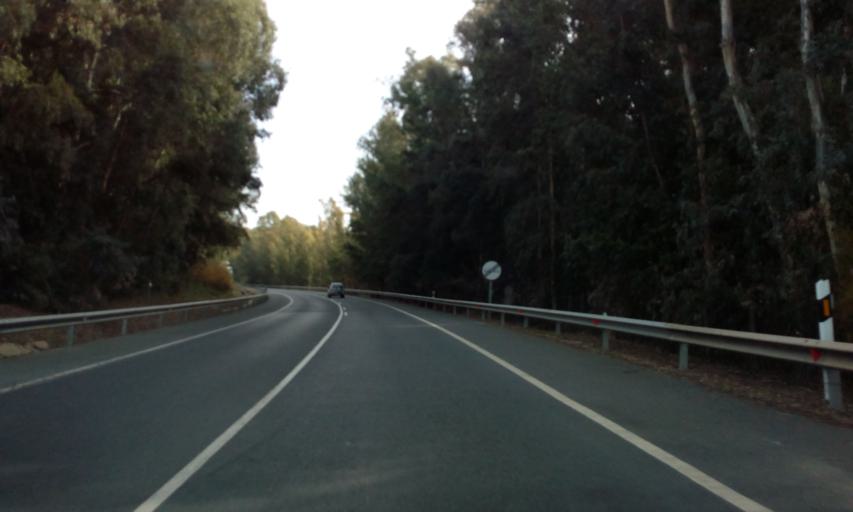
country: ES
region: Andalusia
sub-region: Provincia de Huelva
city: Palos de la Frontera
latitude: 37.1633
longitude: -6.8883
